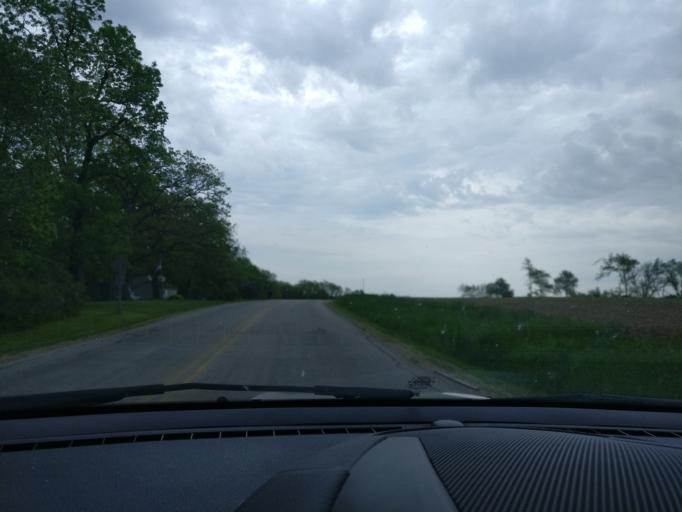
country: US
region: Wisconsin
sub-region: Lafayette County
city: Darlington
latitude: 42.7488
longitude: -89.9847
